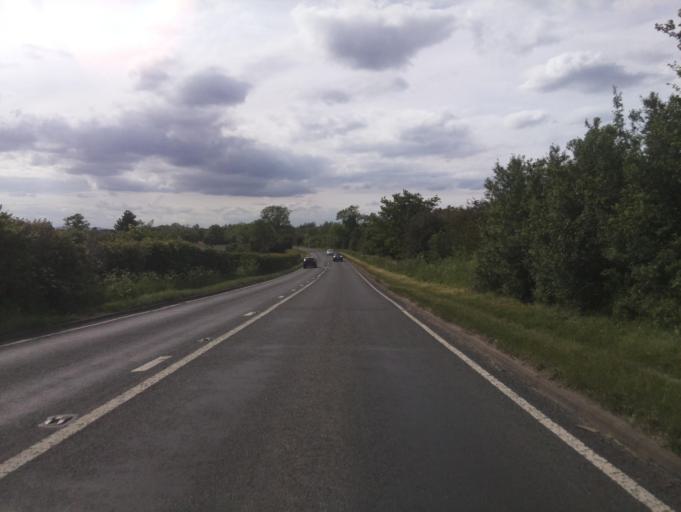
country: GB
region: England
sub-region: Worcestershire
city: Evesham
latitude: 52.0921
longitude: -1.9869
